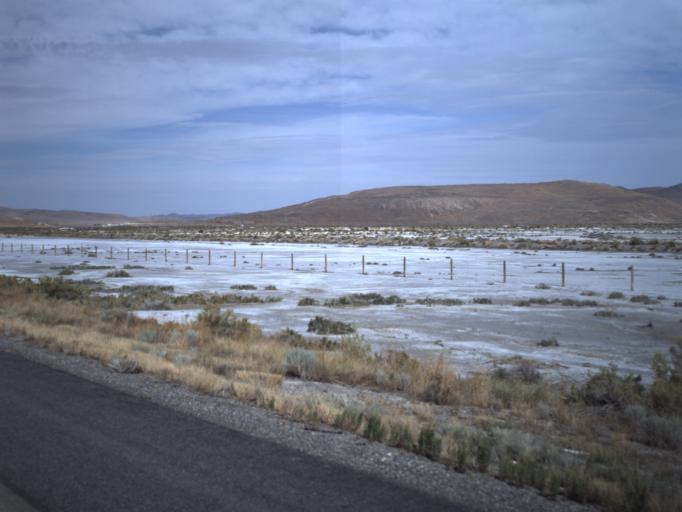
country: US
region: Utah
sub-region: Tooele County
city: Grantsville
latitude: 40.7565
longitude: -112.7570
